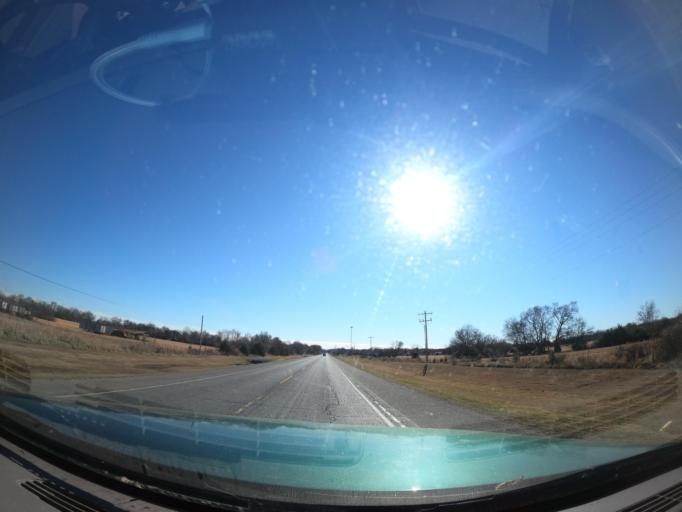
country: US
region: Oklahoma
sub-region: Muskogee County
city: Haskell
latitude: 35.8313
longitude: -95.6775
